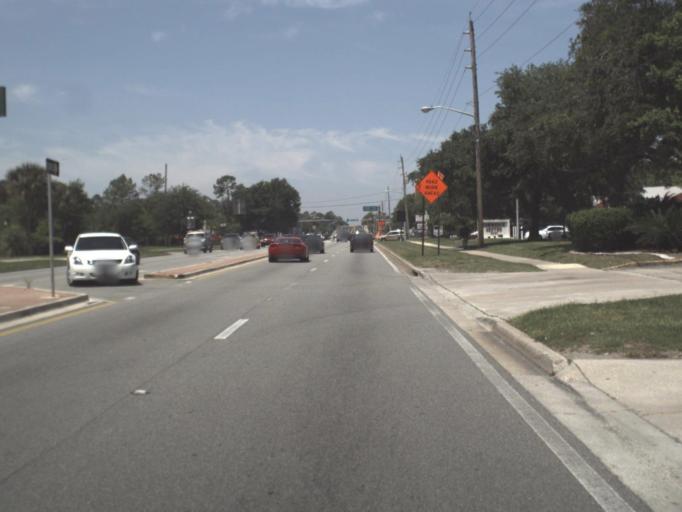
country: US
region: Florida
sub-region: Saint Johns County
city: Fruit Cove
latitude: 30.2209
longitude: -81.5794
